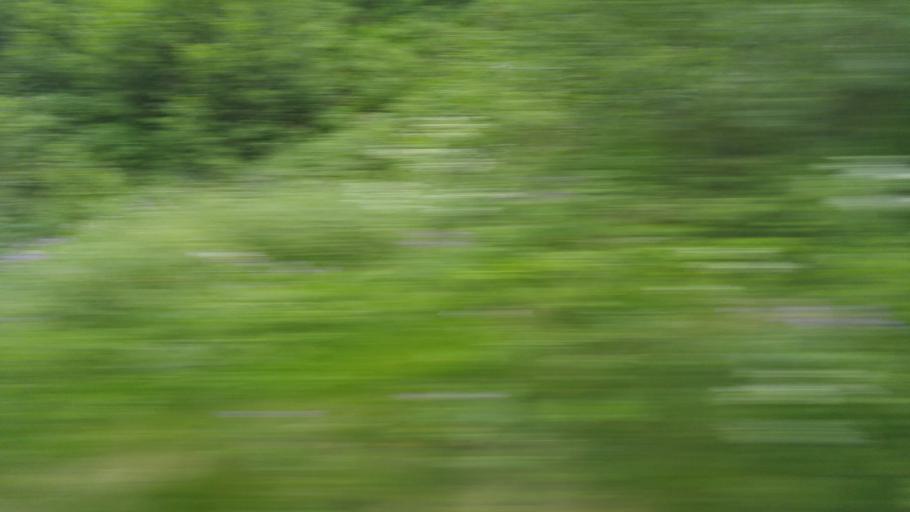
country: NO
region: Nord-Trondelag
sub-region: Levanger
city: Skogn
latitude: 63.4584
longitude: 11.3096
